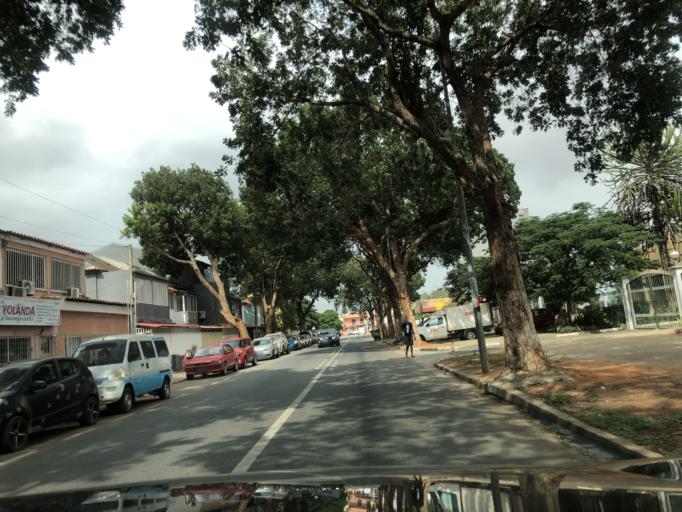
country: AO
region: Luanda
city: Luanda
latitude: -8.8279
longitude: 13.2465
